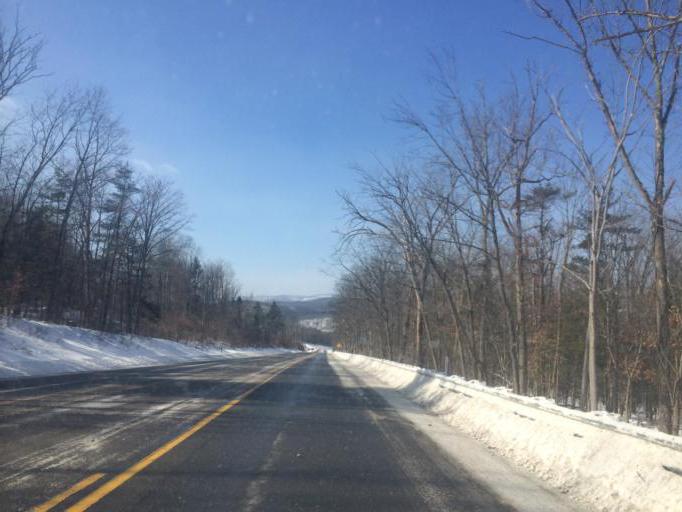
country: US
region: Pennsylvania
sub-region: Centre County
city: Stormstown
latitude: 40.8283
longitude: -78.0011
